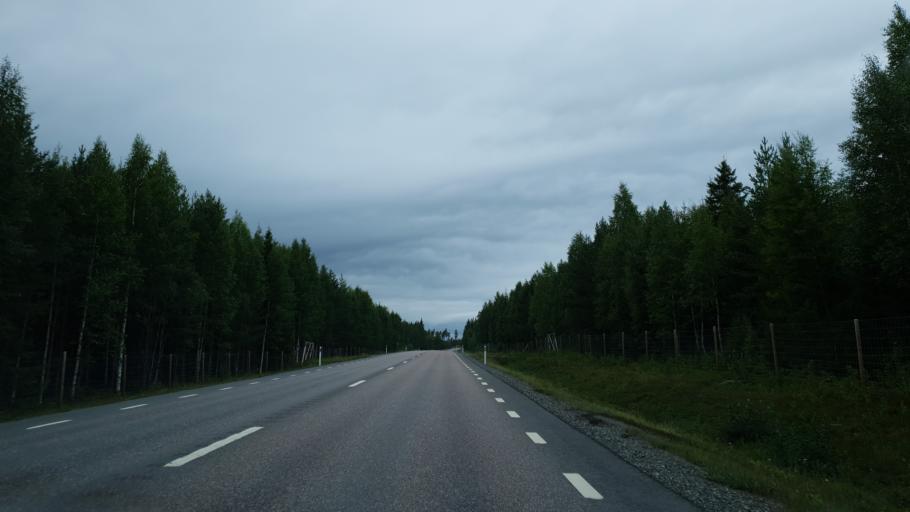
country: SE
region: Vaesterbotten
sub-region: Skelleftea Kommun
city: Viken
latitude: 64.7900
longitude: 20.7678
